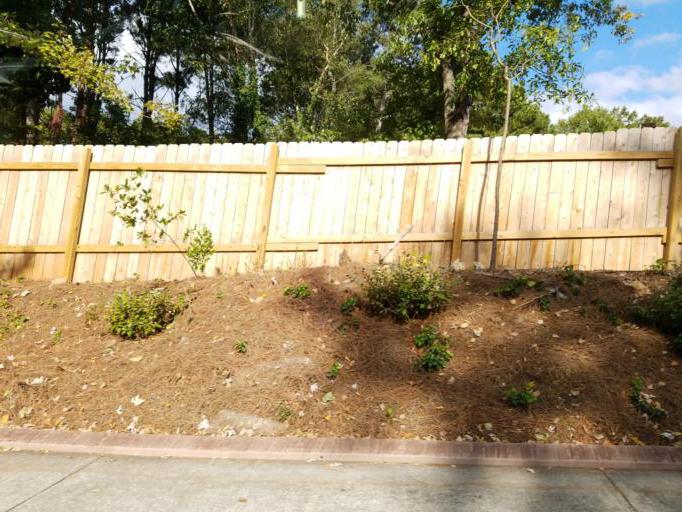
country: US
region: Georgia
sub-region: Cobb County
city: Smyrna
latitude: 33.9291
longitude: -84.4733
